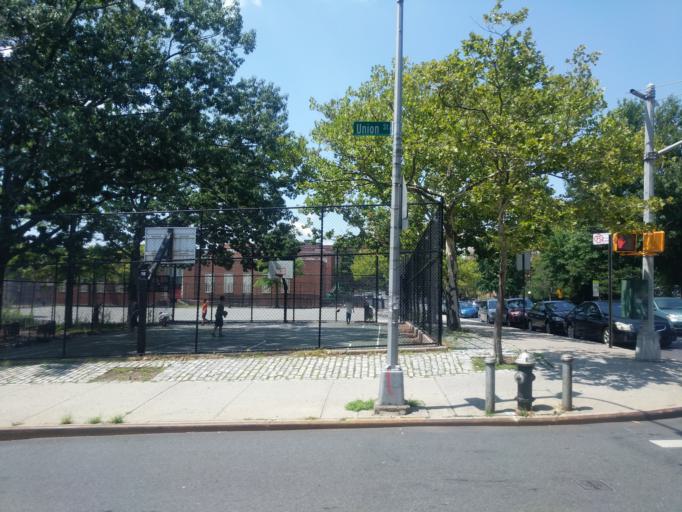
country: US
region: New York
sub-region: Queens County
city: Jamaica
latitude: 40.7705
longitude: -73.8268
